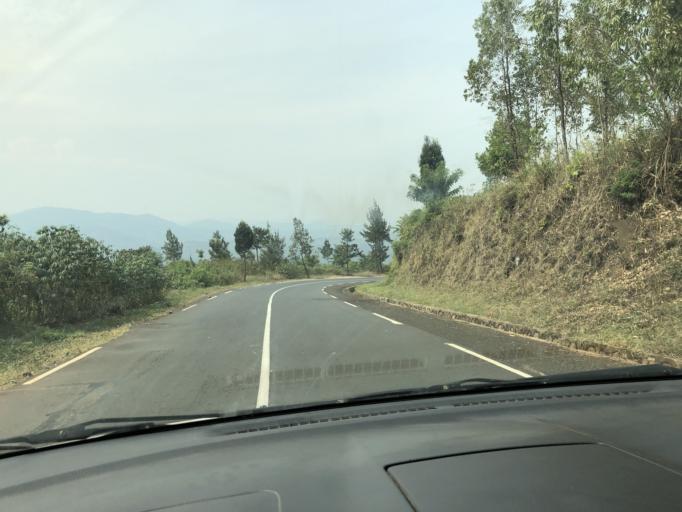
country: RW
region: Western Province
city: Cyangugu
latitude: -2.6701
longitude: 29.0028
